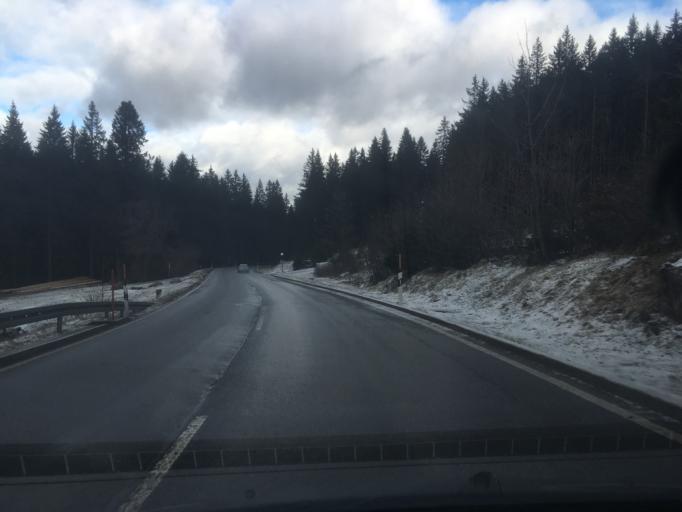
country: DE
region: Baden-Wuerttemberg
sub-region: Freiburg Region
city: Hinterzarten
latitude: 47.8602
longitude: 8.0673
